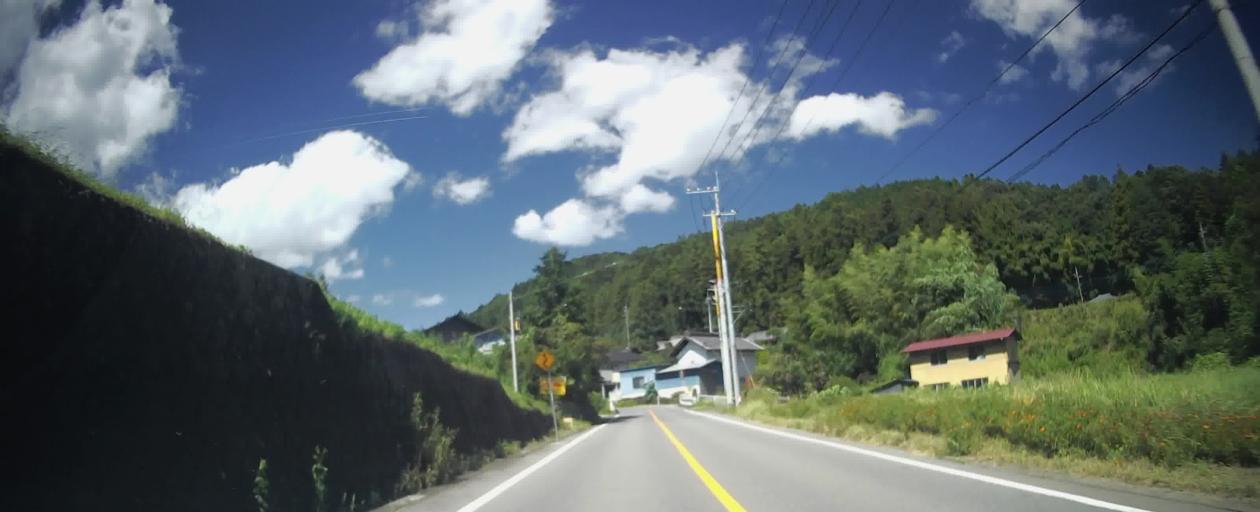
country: JP
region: Gunma
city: Kanekomachi
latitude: 36.4227
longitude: 138.9347
